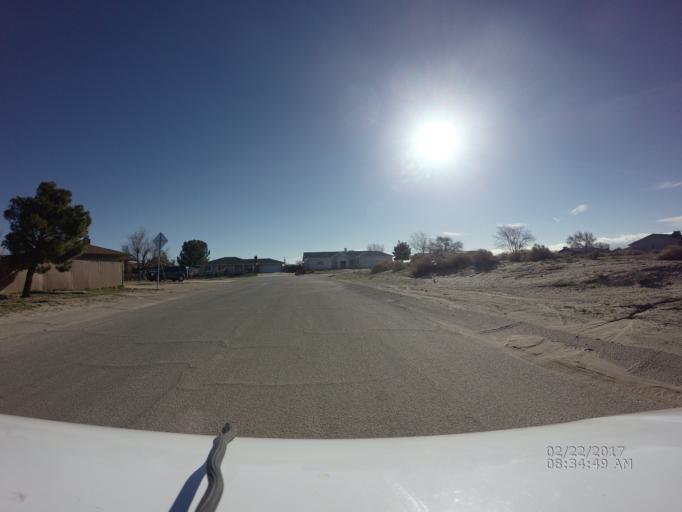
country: US
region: California
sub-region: Los Angeles County
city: Lake Los Angeles
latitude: 34.6347
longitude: -117.8529
